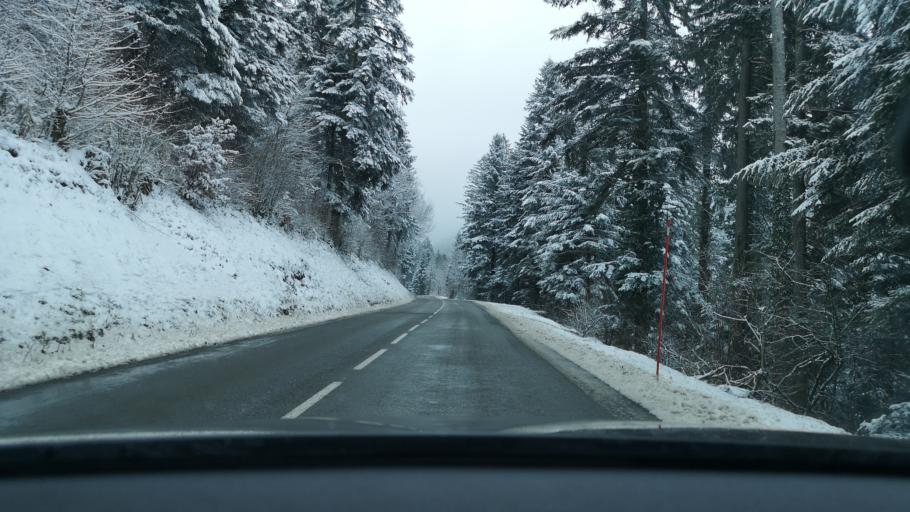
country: FR
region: Rhone-Alpes
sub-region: Departement de l'Ain
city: Oyonnax
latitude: 46.2532
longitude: 5.6775
